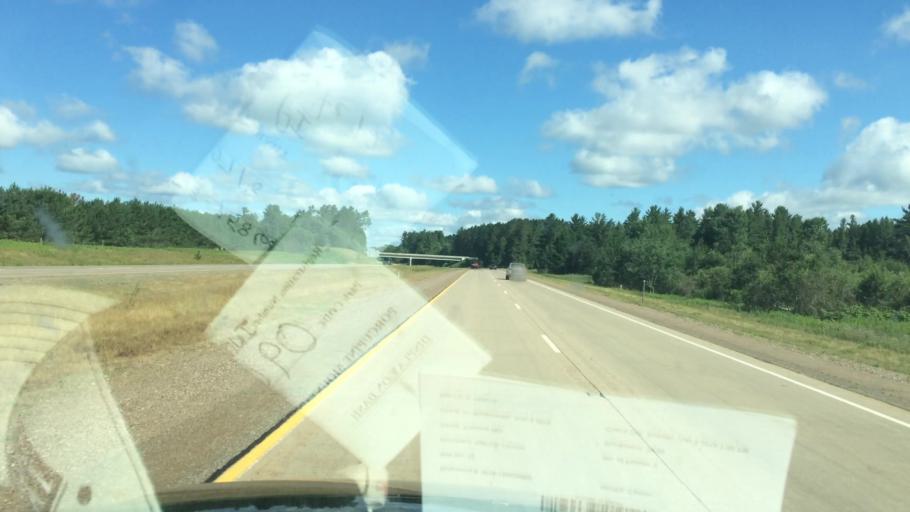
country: US
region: Wisconsin
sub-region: Lincoln County
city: Tomahawk
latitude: 45.4331
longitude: -89.6794
